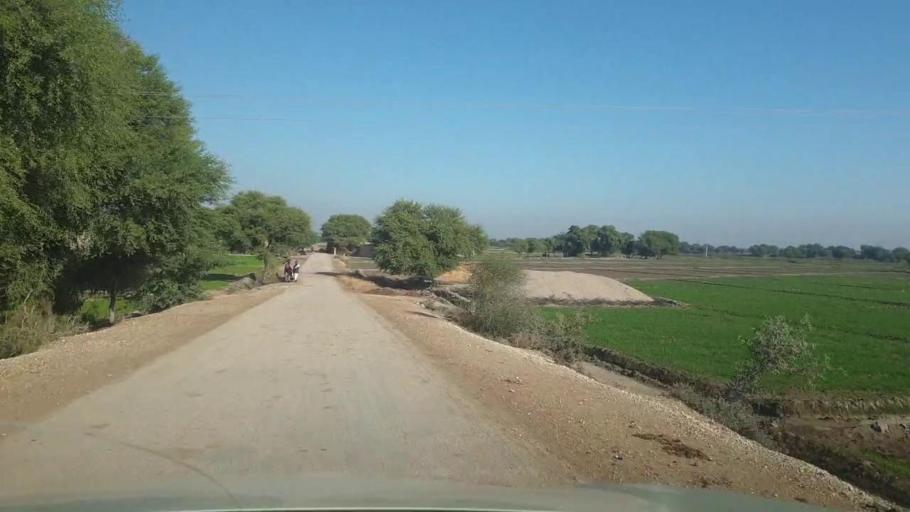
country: PK
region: Sindh
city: Bhan
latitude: 26.5596
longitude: 67.6640
